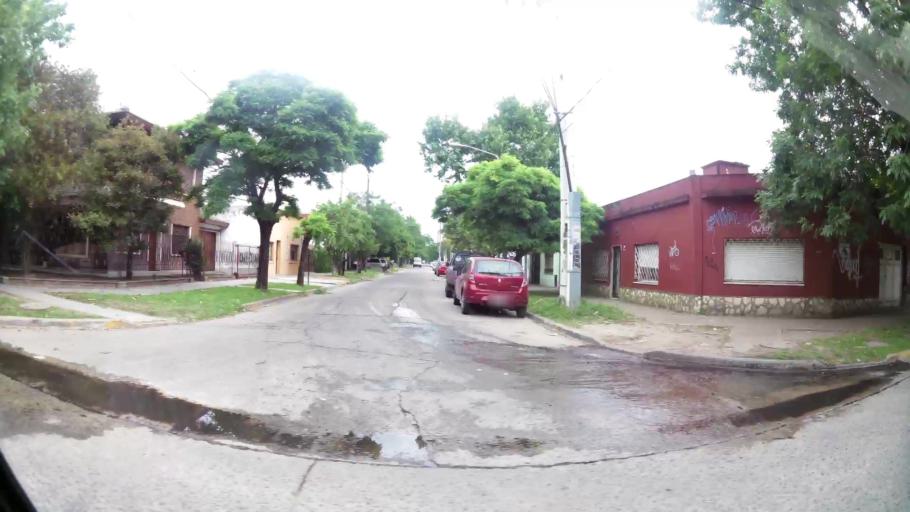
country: AR
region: Buenos Aires
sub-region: Partido de Ezeiza
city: Ezeiza
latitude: -34.8583
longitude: -58.5205
